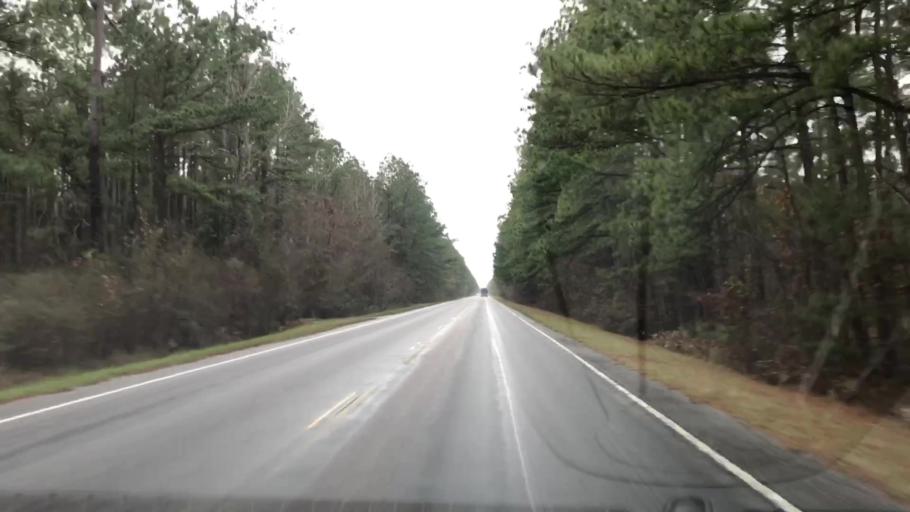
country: US
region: South Carolina
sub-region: Berkeley County
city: Saint Stephen
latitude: 33.2874
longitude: -79.8394
